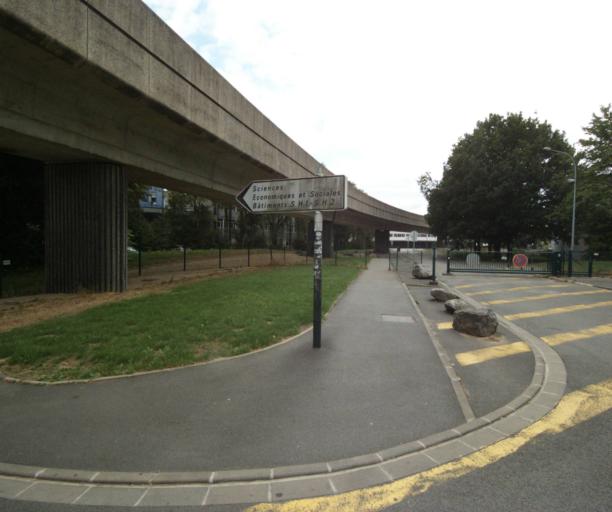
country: FR
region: Nord-Pas-de-Calais
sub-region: Departement du Nord
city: Villeneuve-d'Ascq
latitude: 50.6113
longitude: 3.1422
